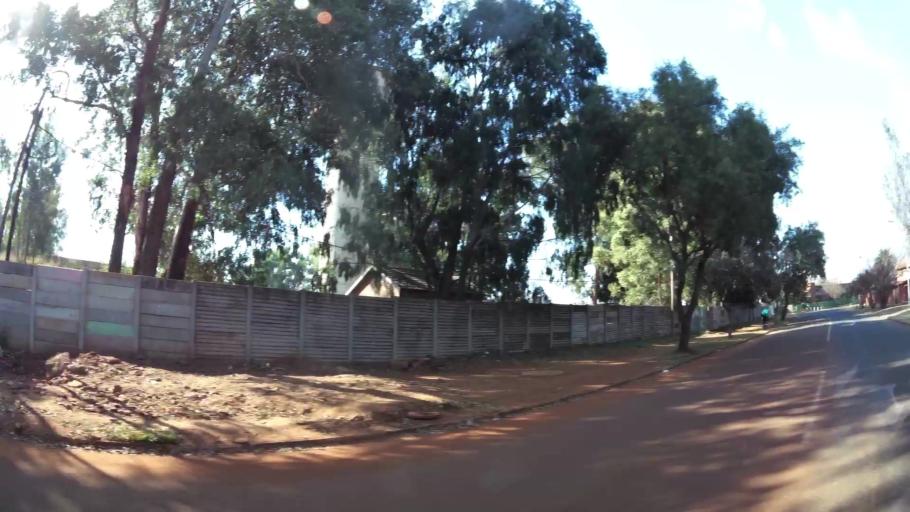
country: ZA
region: Gauteng
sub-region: West Rand District Municipality
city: Randfontein
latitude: -26.1657
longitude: 27.7028
